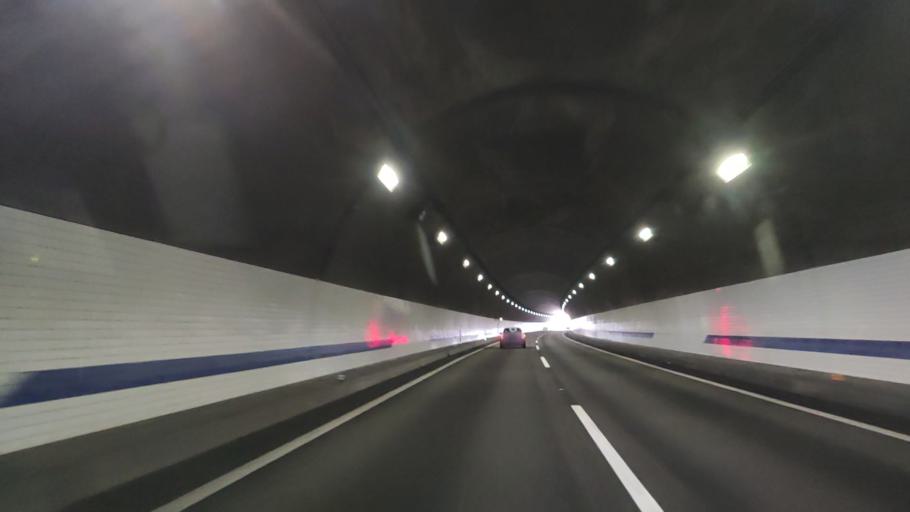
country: JP
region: Tokushima
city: Ishii
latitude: 34.1738
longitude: 134.4469
